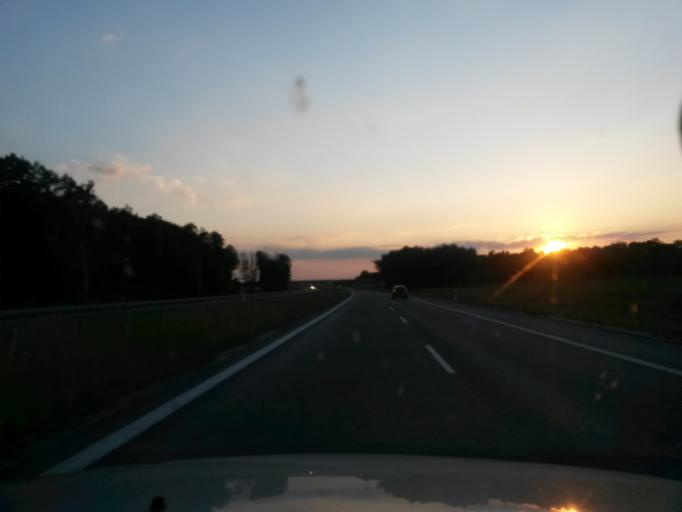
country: PL
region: Lodz Voivodeship
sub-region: Powiat wieruszowski
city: Wieruszow
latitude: 51.3373
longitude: 18.1288
